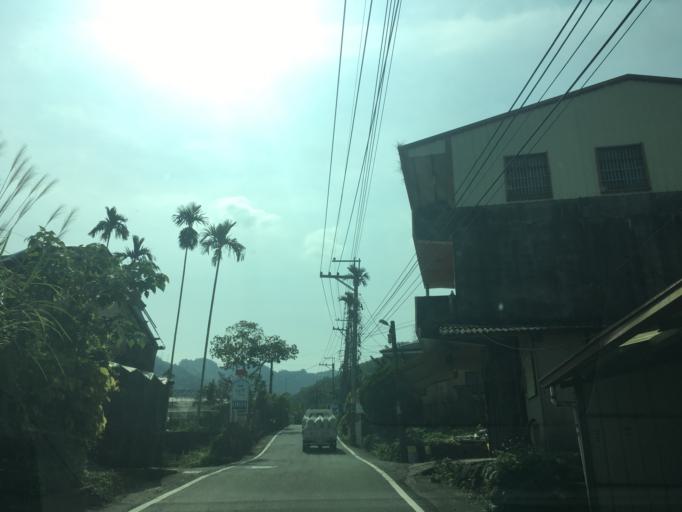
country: TW
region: Taiwan
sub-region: Taichung City
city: Taichung
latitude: 24.1571
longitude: 120.8286
